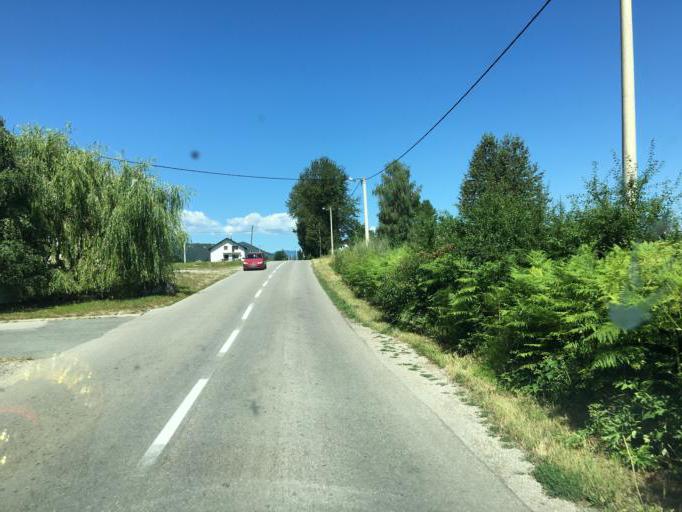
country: HR
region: Licko-Senjska
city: Gospic
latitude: 44.5579
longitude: 15.3341
